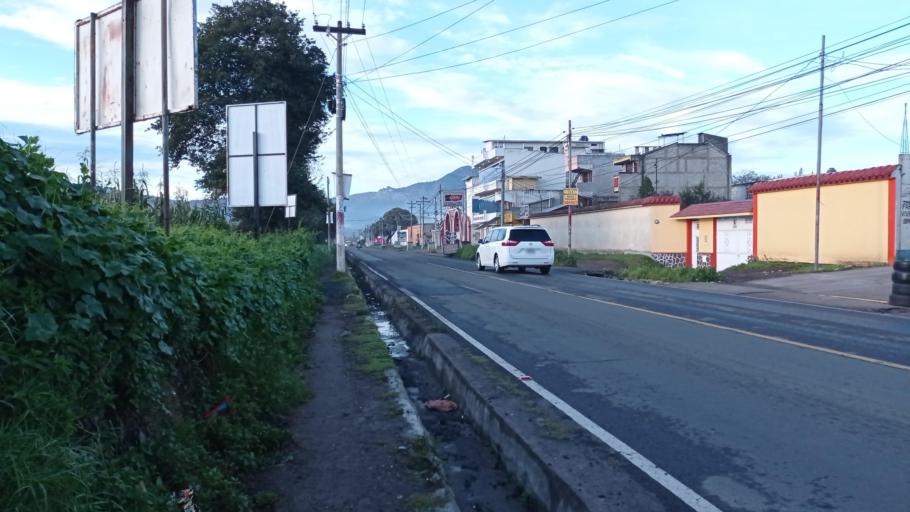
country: GT
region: Quetzaltenango
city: Olintepeque
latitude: 14.8650
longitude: -91.5125
